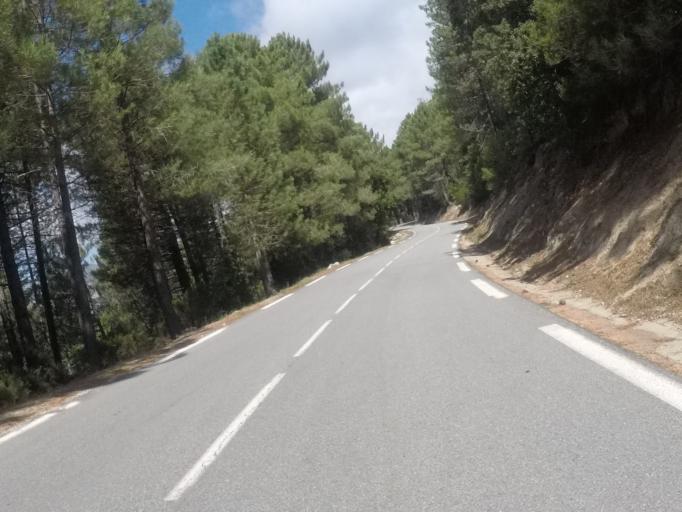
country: FR
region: Corsica
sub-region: Departement de la Corse-du-Sud
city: Zonza
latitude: 41.7650
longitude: 9.2073
